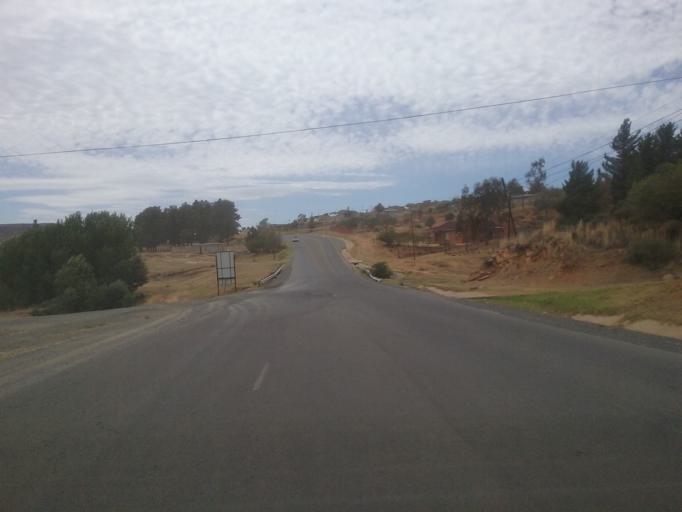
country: LS
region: Maseru
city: Nako
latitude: -29.6303
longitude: 27.4834
